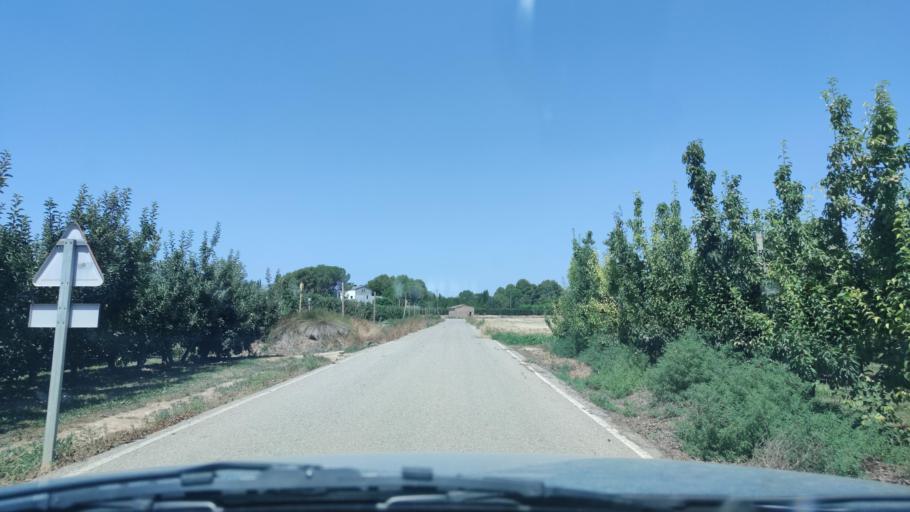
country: ES
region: Catalonia
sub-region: Provincia de Lleida
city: Torrefarrera
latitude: 41.6534
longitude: 0.5899
